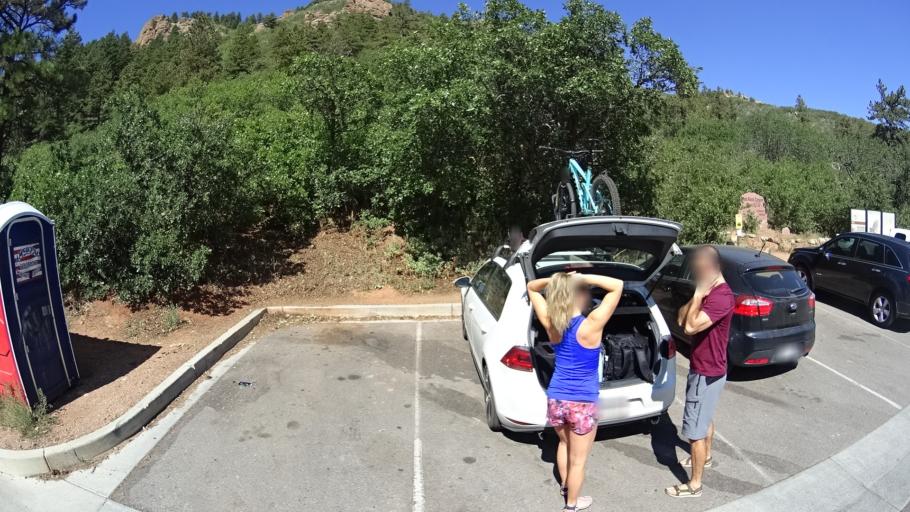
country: US
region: Colorado
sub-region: El Paso County
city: Manitou Springs
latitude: 38.8228
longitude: -104.8903
